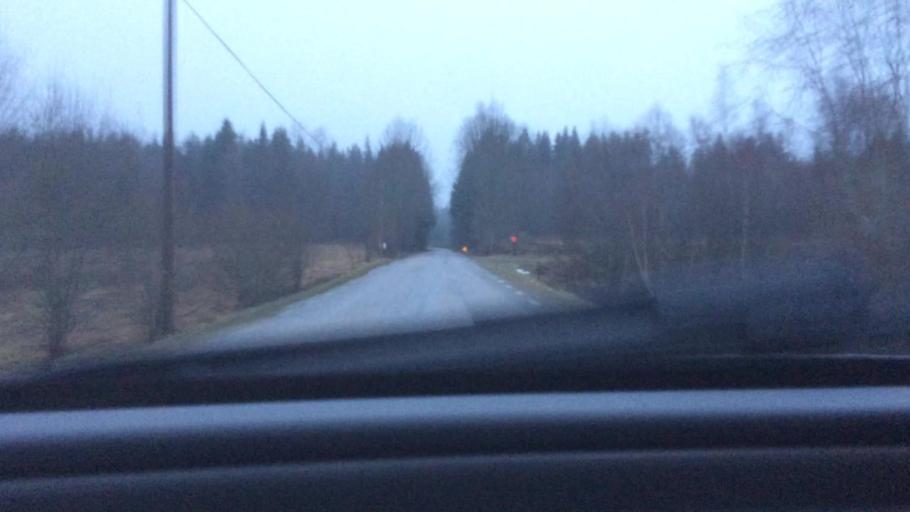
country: SE
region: Vaestra Goetaland
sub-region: Ulricehamns Kommun
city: Ulricehamn
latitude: 57.9621
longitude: 13.3974
